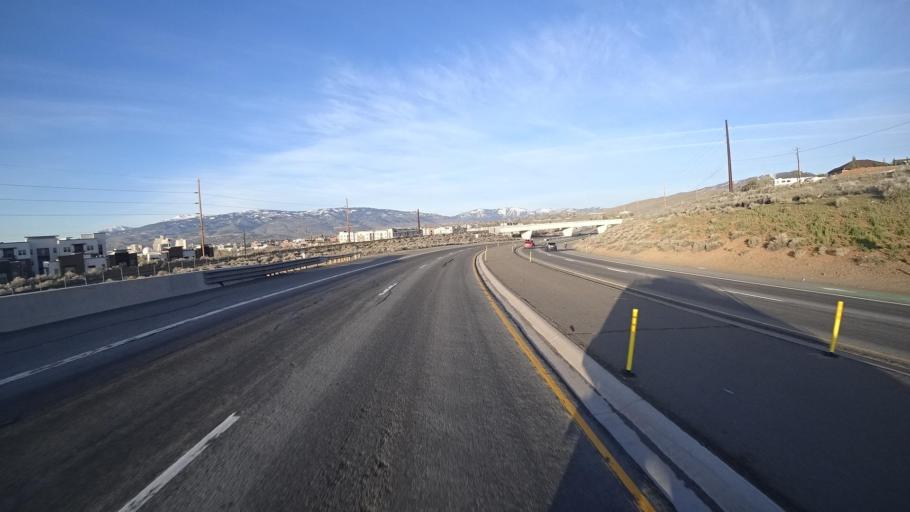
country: US
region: Nevada
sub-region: Washoe County
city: Reno
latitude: 39.5524
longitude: -119.8059
